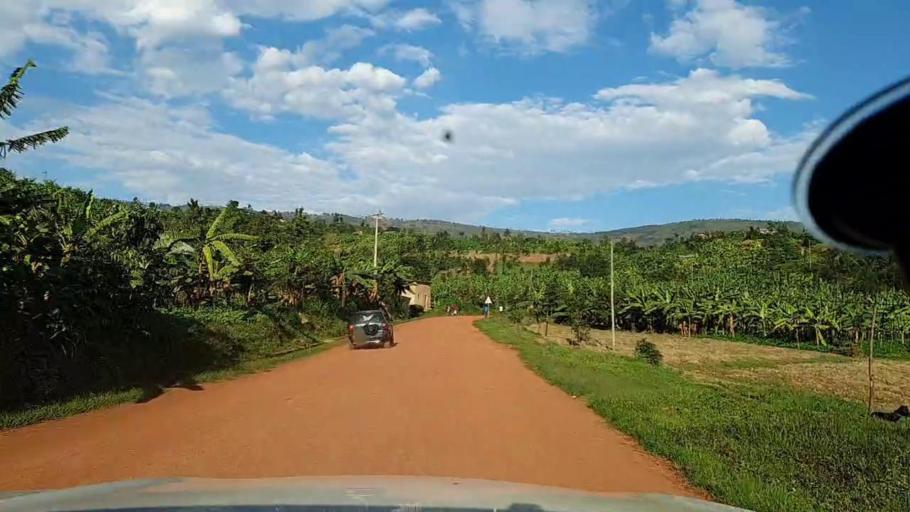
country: RW
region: Kigali
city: Kigali
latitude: -1.8640
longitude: 29.9220
